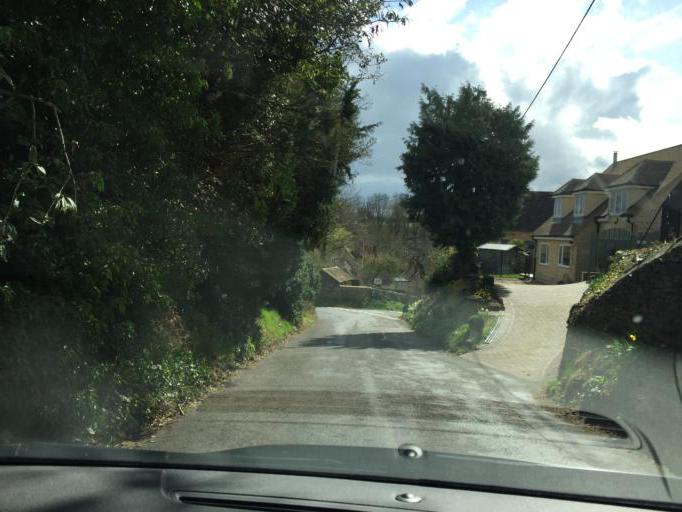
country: GB
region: England
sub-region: Oxfordshire
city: Woodstock
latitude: 51.8745
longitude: -1.3639
